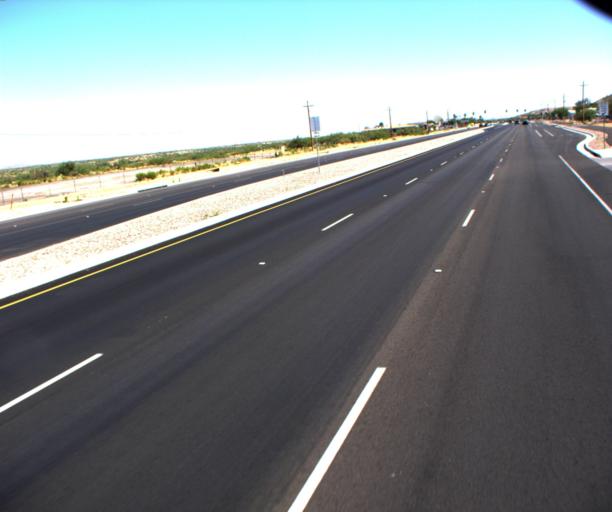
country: US
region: Arizona
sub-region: Pima County
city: Catalina
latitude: 32.5045
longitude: -110.9258
